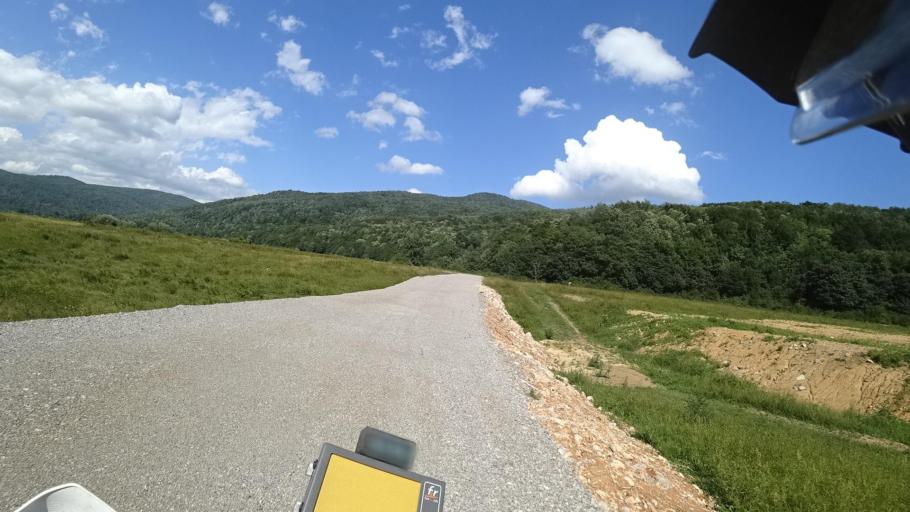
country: HR
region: Licko-Senjska
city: Brinje
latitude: 45.1429
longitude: 15.1093
